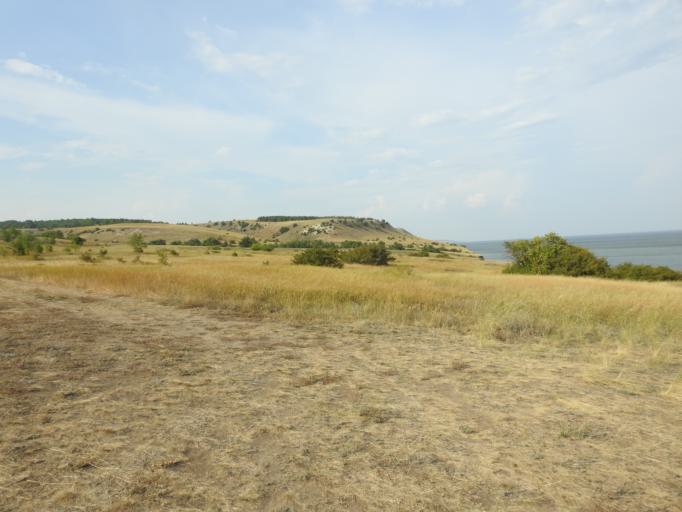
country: RU
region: Volgograd
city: Kamyshin
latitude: 50.2523
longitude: 45.6544
